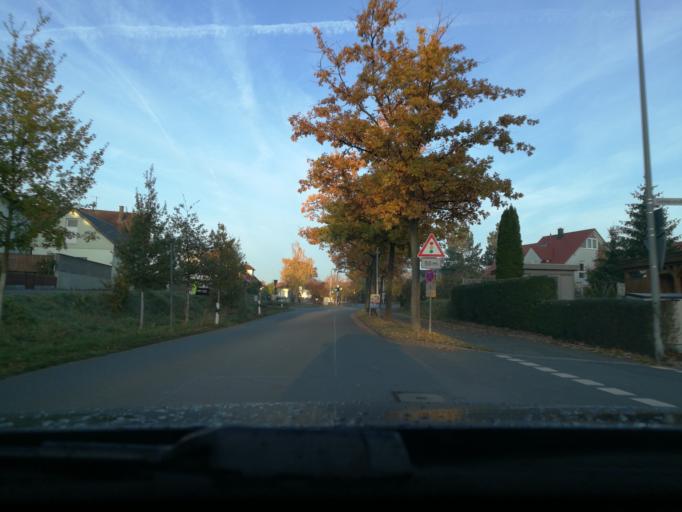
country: DE
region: Bavaria
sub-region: Regierungsbezirk Mittelfranken
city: Herzogenaurach
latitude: 49.5670
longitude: 10.9154
